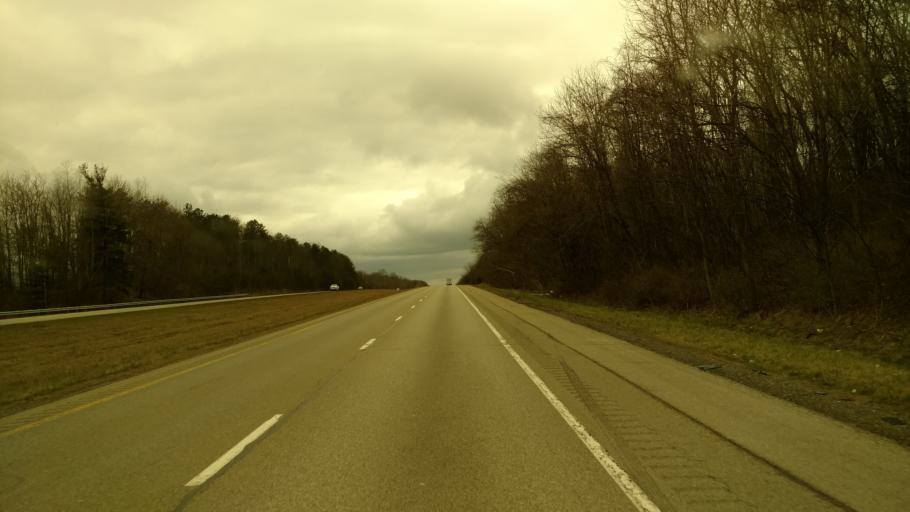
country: US
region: Ohio
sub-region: Muskingum County
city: Zanesville
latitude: 39.9453
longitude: -82.1019
